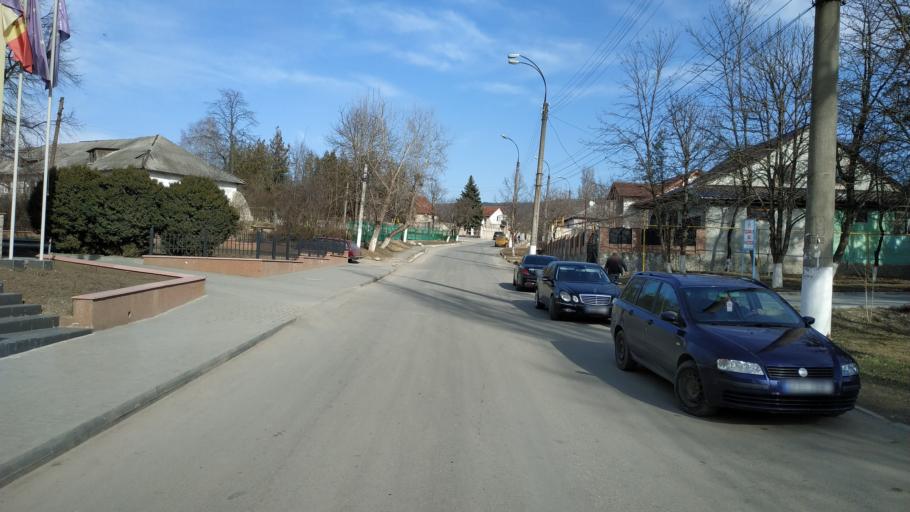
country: MD
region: Nisporeni
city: Nisporeni
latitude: 47.0799
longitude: 28.1894
